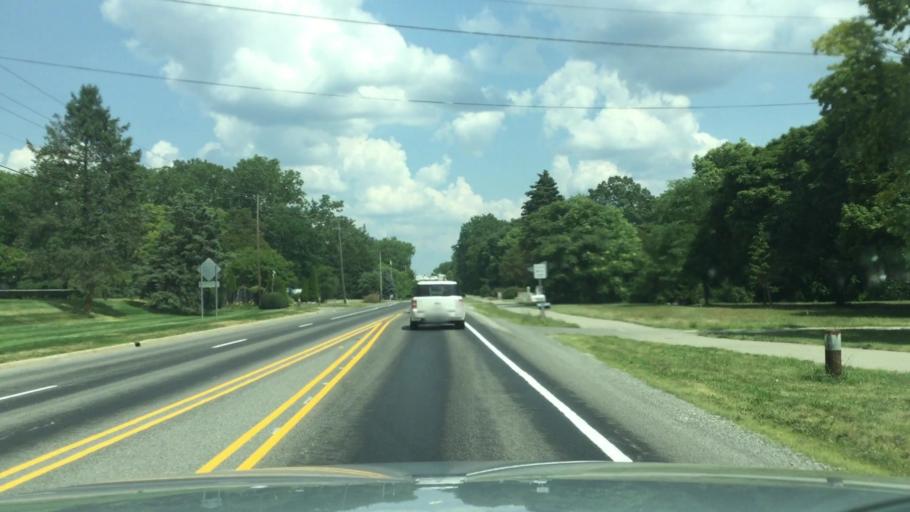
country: US
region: Michigan
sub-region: Washtenaw County
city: Ypsilanti
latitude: 42.2028
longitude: -83.5690
